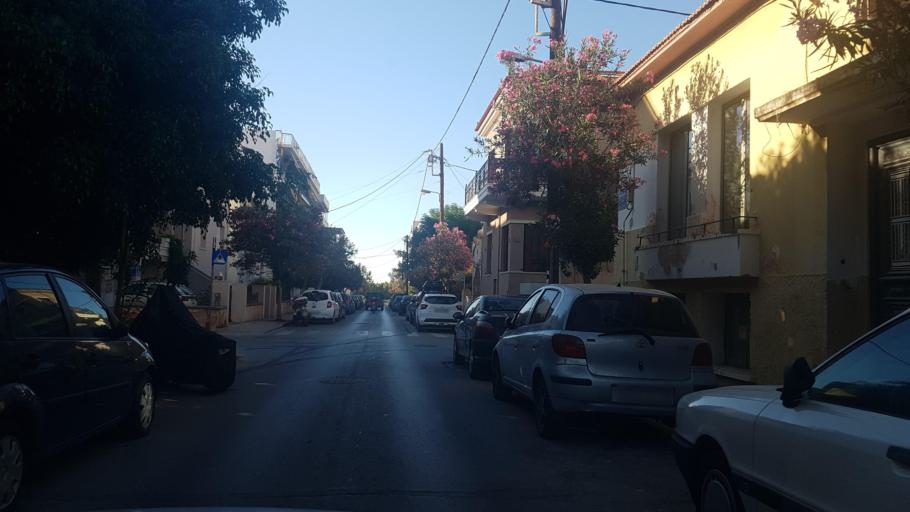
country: GR
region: Crete
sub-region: Nomos Chanias
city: Chania
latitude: 35.5157
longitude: 24.0132
